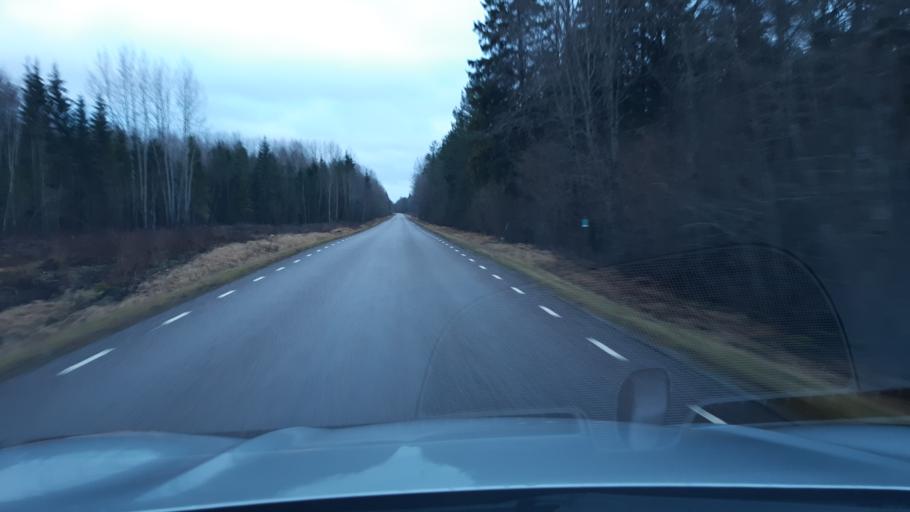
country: EE
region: Raplamaa
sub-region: Kohila vald
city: Kohila
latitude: 59.1383
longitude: 24.6577
